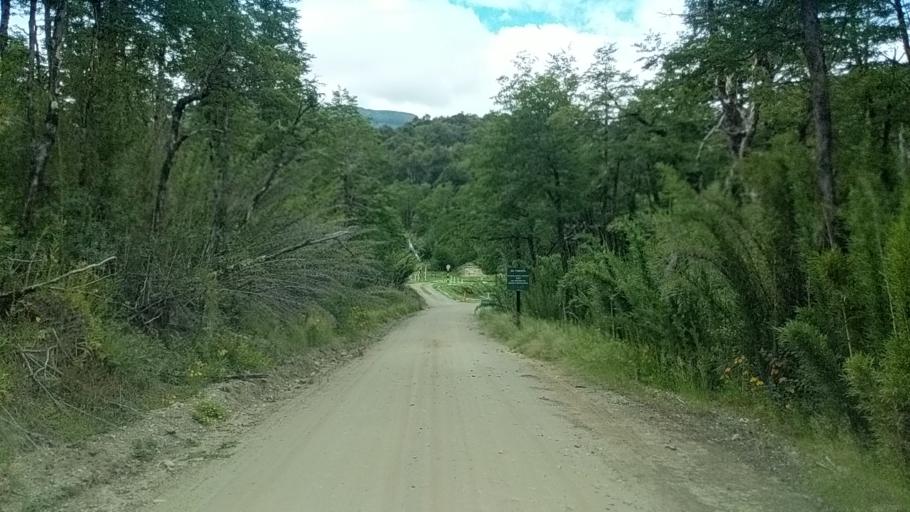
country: AR
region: Neuquen
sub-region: Departamento de Lacar
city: San Martin de los Andes
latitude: -39.8242
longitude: -71.6416
